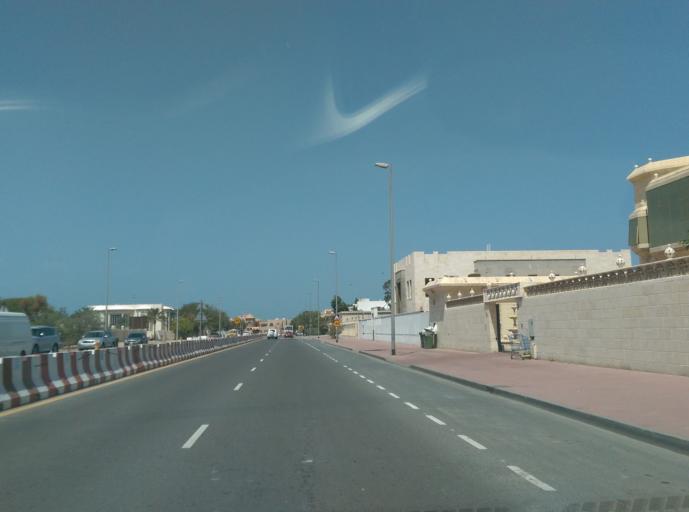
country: AE
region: Dubai
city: Dubai
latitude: 25.1871
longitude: 55.2376
